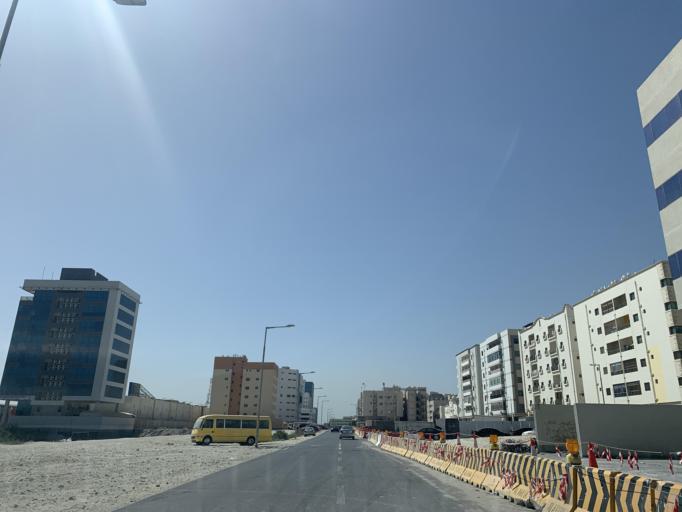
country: BH
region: Northern
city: Ar Rifa'
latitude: 26.1385
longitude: 50.5812
